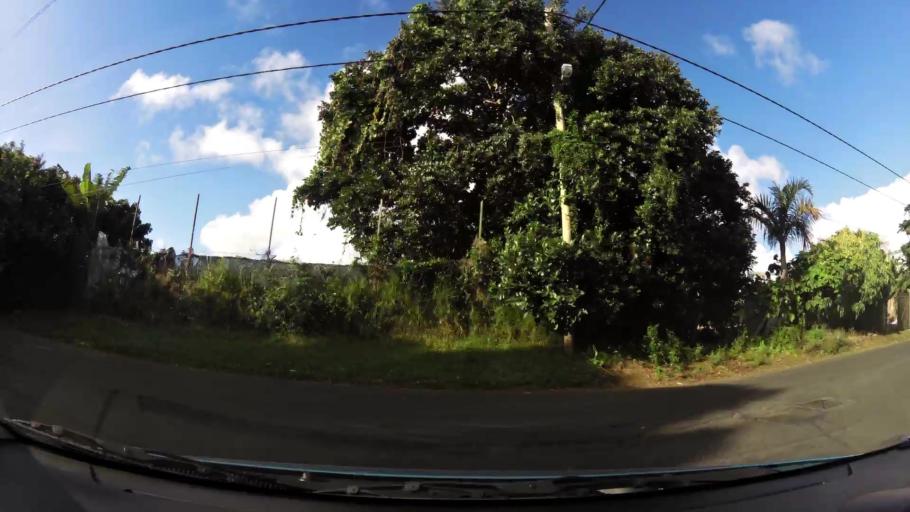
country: MU
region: Plaines Wilhems
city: Vacoas
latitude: -20.3072
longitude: 57.4984
